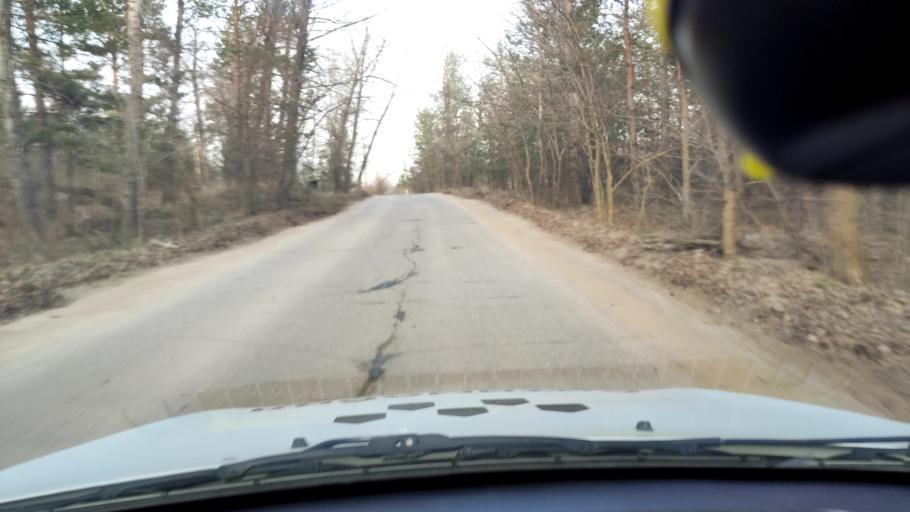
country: RU
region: Samara
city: Zhigulevsk
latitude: 53.4536
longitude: 49.5689
